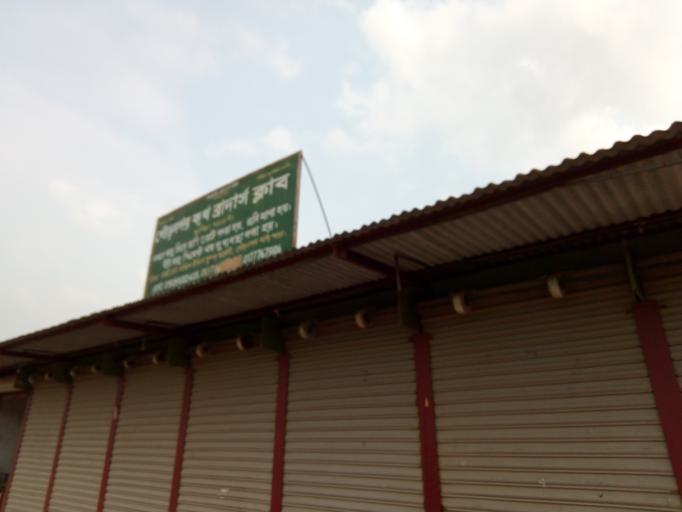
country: BD
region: Dhaka
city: Paltan
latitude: 23.7603
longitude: 90.4708
